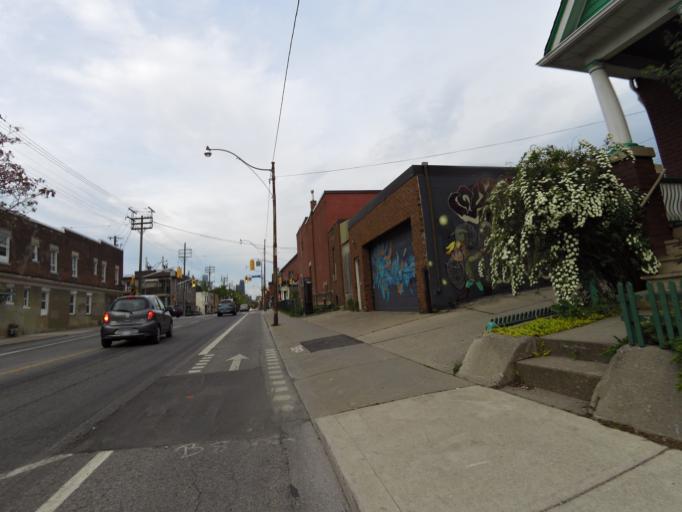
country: CA
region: Ontario
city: Toronto
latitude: 43.6601
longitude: -79.4165
